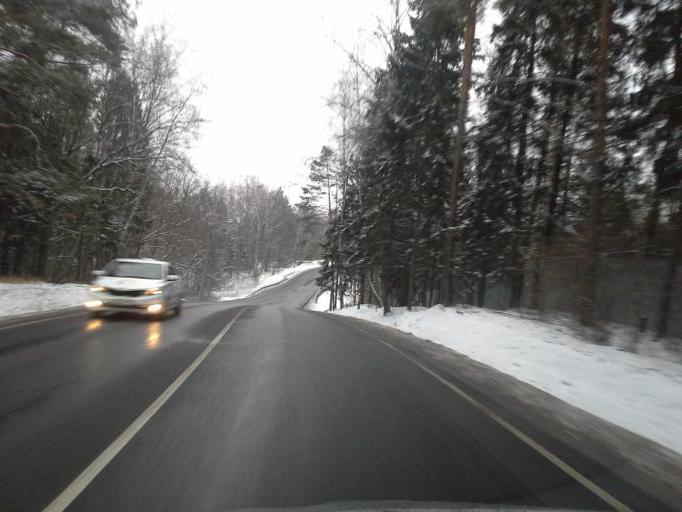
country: RU
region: Moskovskaya
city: Nikolina Gora
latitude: 55.7075
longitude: 37.0921
